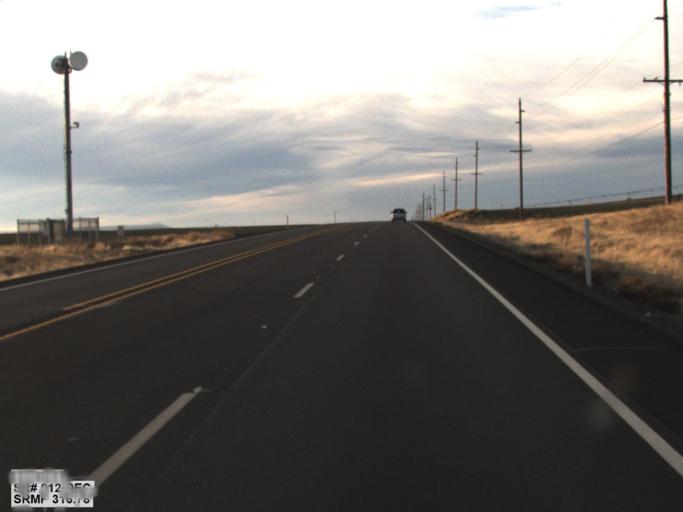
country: US
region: Washington
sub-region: Walla Walla County
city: Burbank
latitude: 46.0589
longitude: -118.7310
